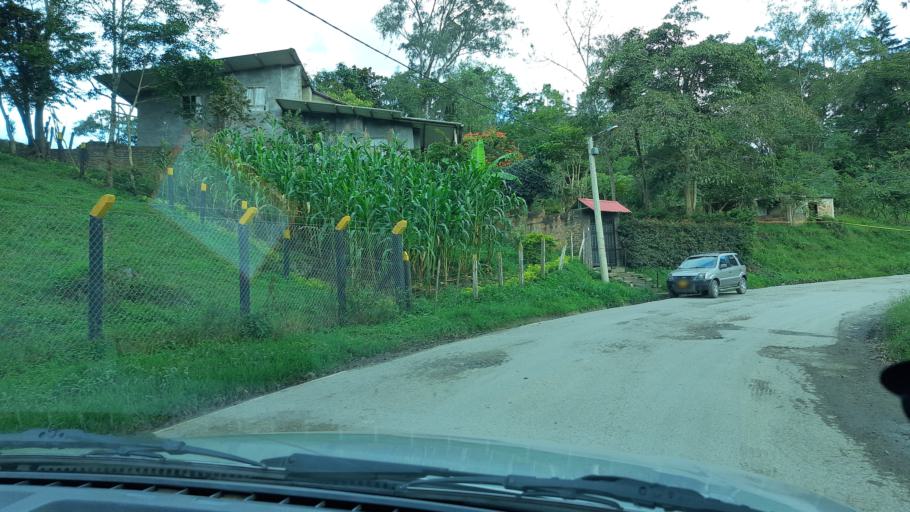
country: CO
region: Boyaca
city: Garagoa
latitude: 5.0896
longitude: -73.3661
